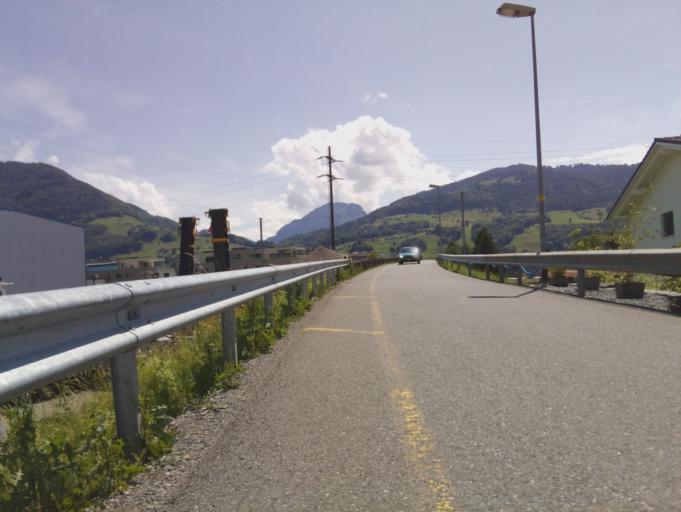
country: CH
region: Schwyz
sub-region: Bezirk March
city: Lachen
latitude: 47.1853
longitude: 8.8921
